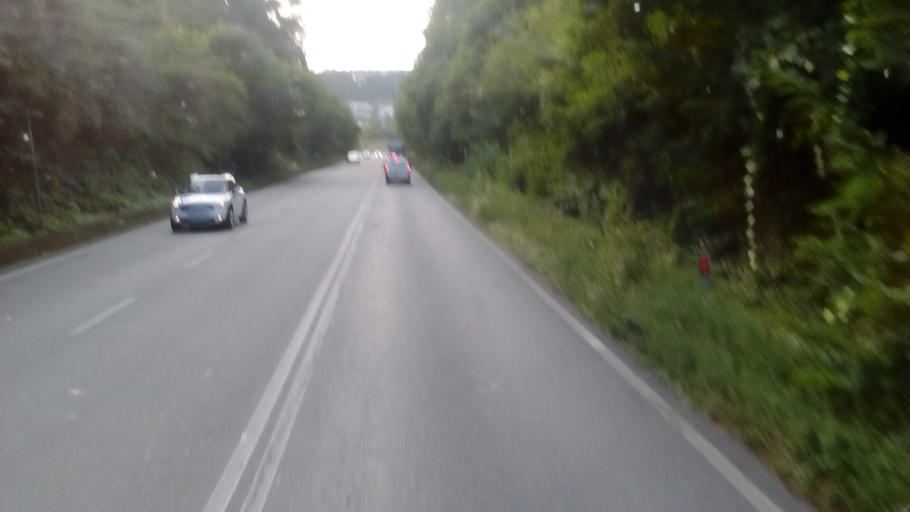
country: IT
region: Lombardy
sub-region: Provincia di Como
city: Novedrate
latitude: 45.6947
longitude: 9.1218
